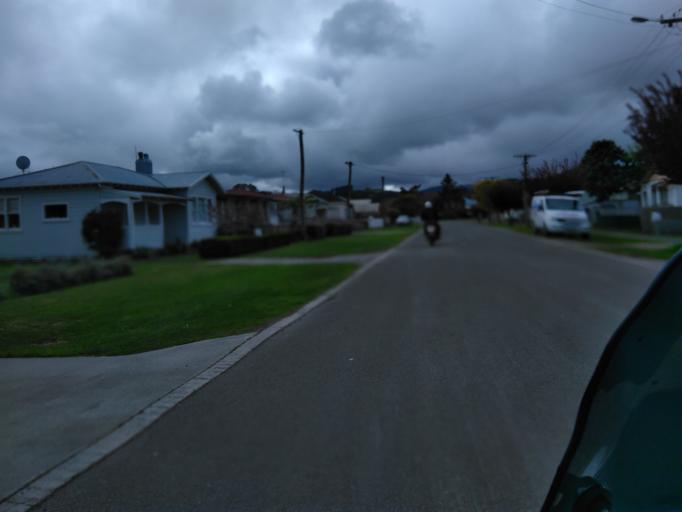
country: NZ
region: Gisborne
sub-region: Gisborne District
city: Gisborne
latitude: -38.6527
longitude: 178.0084
